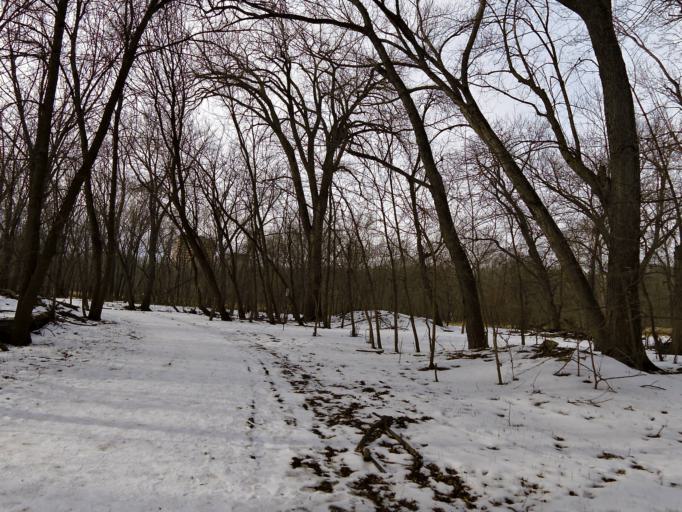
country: US
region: Minnesota
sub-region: Dakota County
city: Eagan
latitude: 44.8562
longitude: -93.2130
